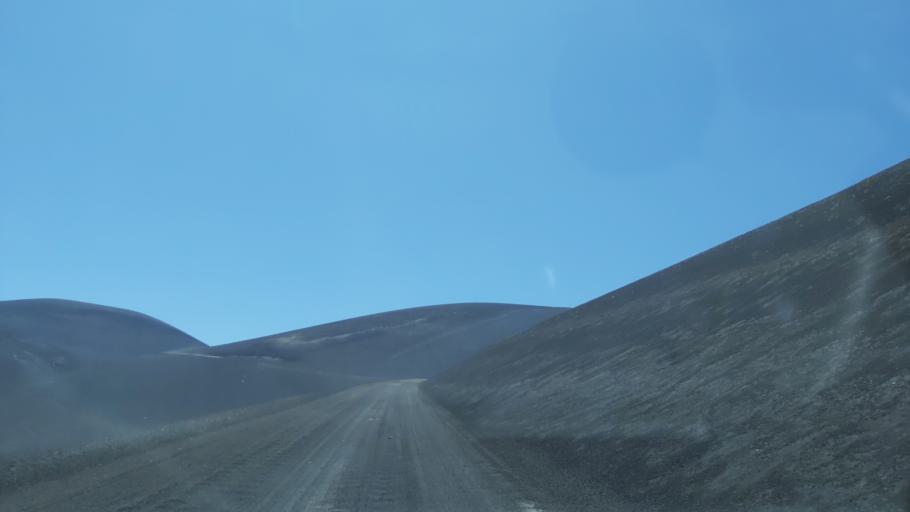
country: CL
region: Araucania
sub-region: Provincia de Cautin
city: Vilcun
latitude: -38.3947
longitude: -71.5457
